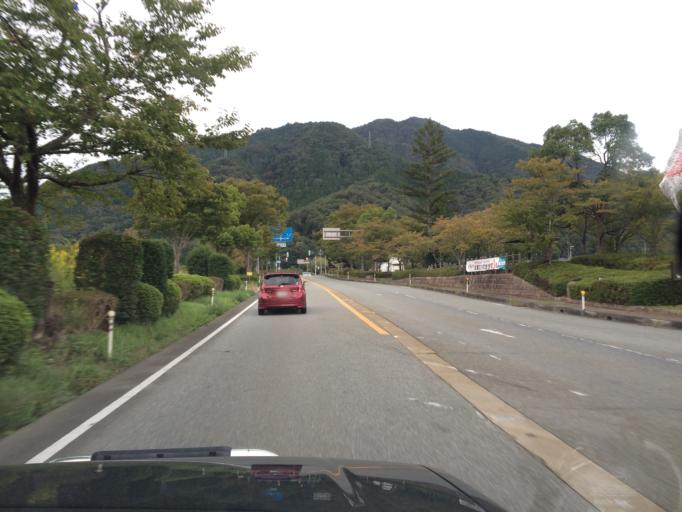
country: JP
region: Hyogo
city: Toyooka
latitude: 35.3831
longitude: 134.8158
